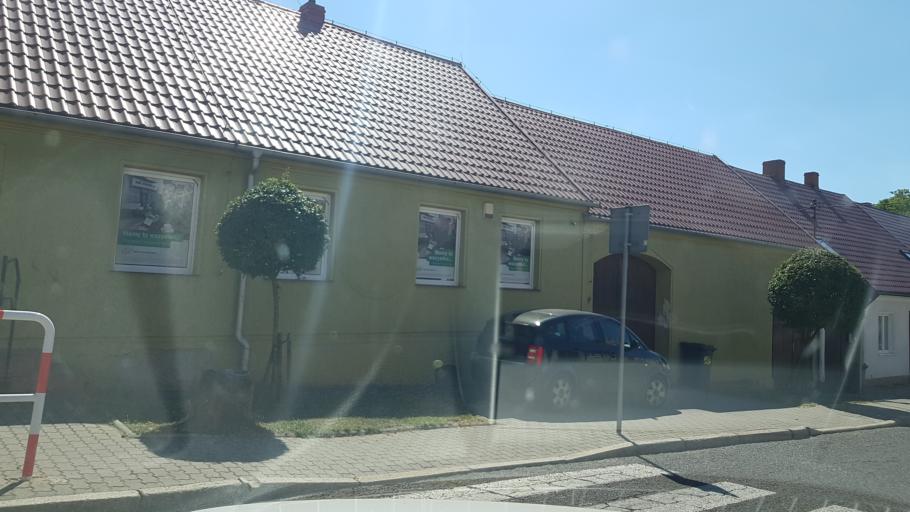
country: PL
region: West Pomeranian Voivodeship
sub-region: Powiat gryfinski
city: Moryn
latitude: 52.8582
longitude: 14.3958
